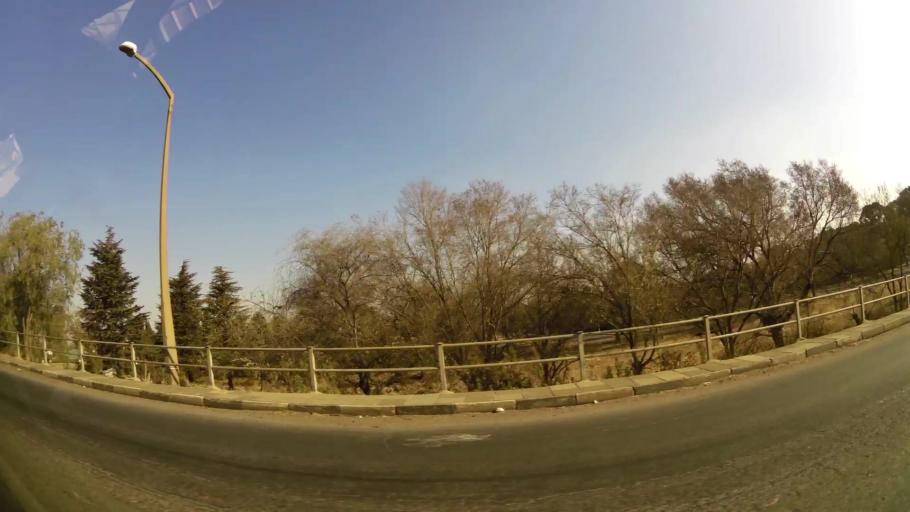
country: ZA
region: Gauteng
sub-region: West Rand District Municipality
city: Randfontein
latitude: -26.1649
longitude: 27.7091
